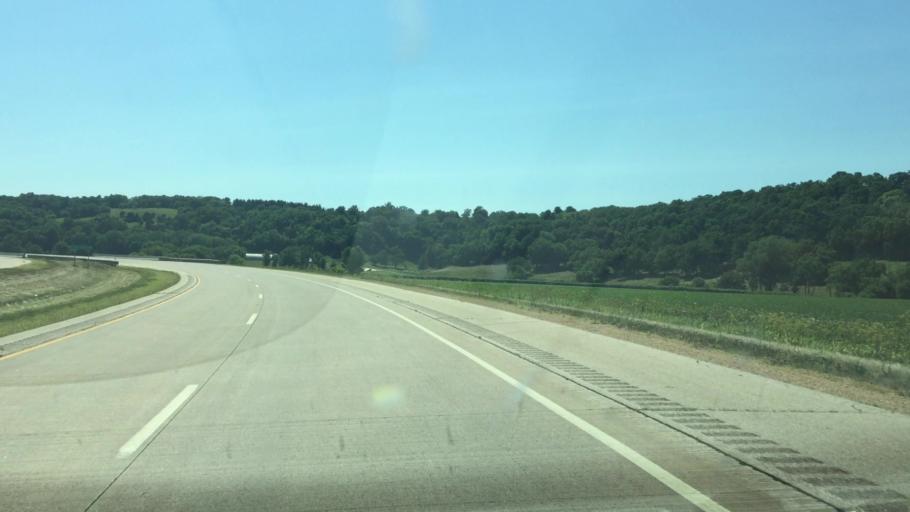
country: US
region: Wisconsin
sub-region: Grant County
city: Dickeyville
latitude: 42.6582
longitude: -90.5696
